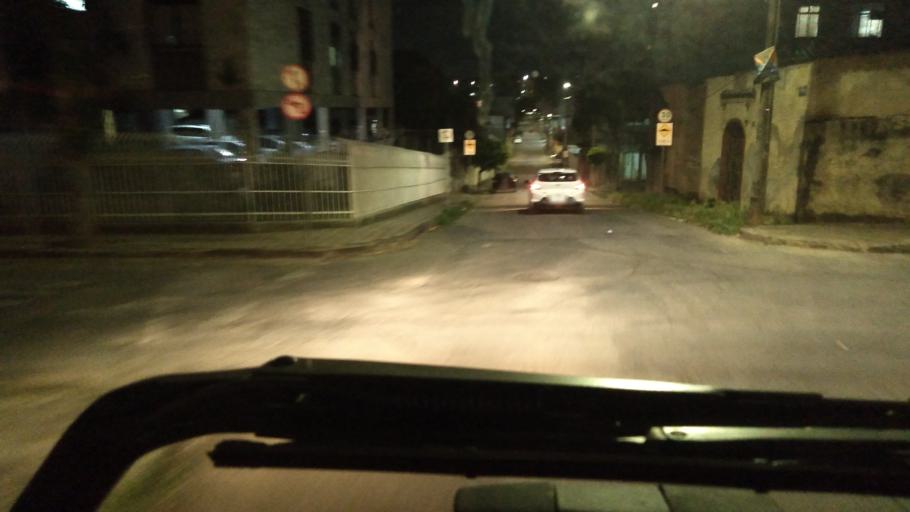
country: BR
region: Minas Gerais
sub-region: Belo Horizonte
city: Belo Horizonte
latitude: -19.9219
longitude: -43.9788
